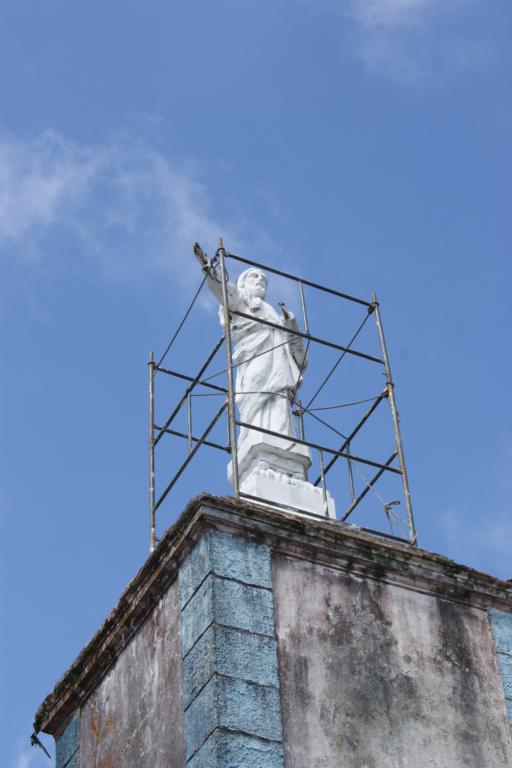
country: BR
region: Sao Paulo
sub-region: Rio Grande Da Serra
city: Rio Grande da Serra
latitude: -23.7691
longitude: -46.3413
